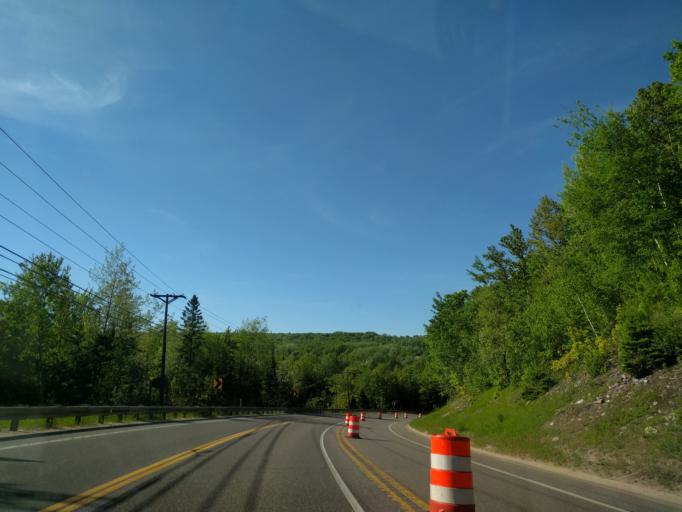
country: US
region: Michigan
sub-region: Marquette County
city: Marquette
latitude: 46.5046
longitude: -87.4273
